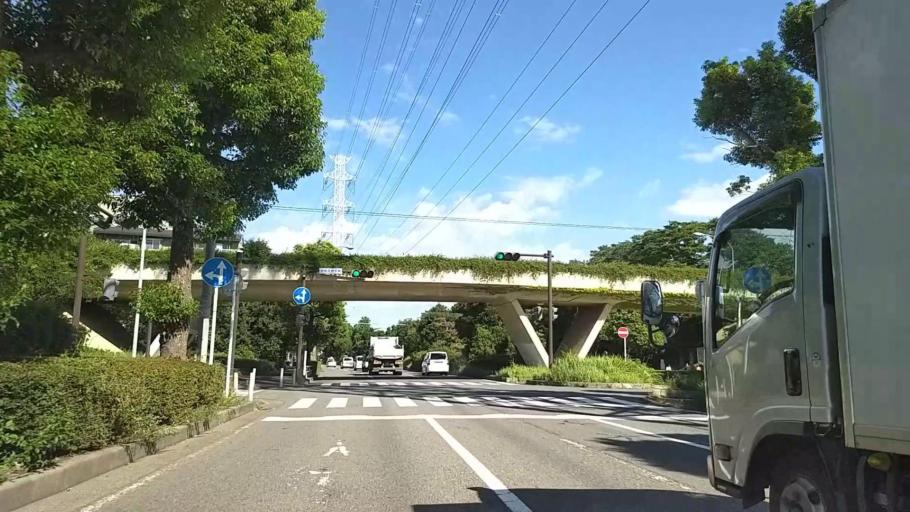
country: JP
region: Tokyo
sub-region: Machida-shi
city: Machida
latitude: 35.5428
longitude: 139.5612
